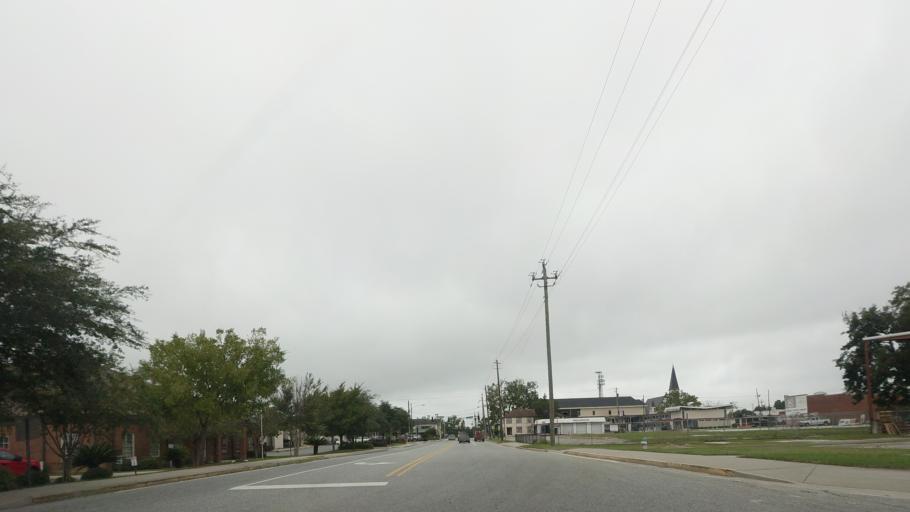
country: US
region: Georgia
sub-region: Lowndes County
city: Valdosta
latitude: 30.8288
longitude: -83.2812
